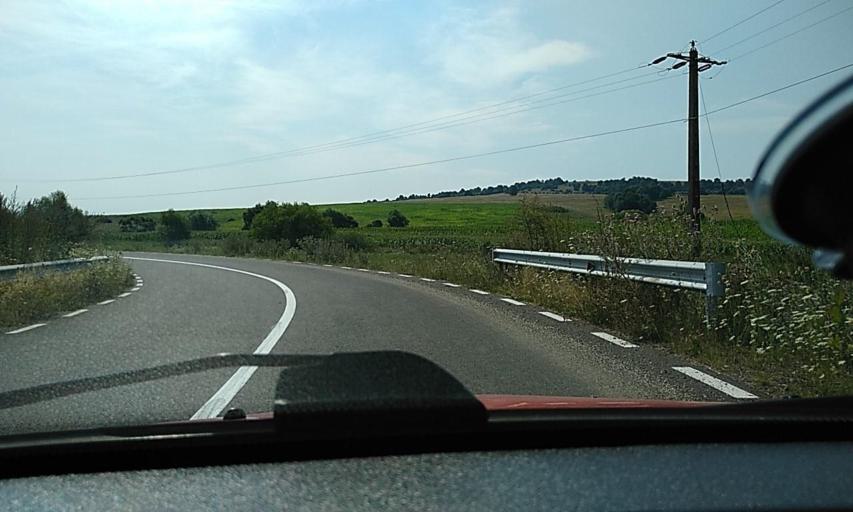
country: RO
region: Brasov
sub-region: Oras Rupea
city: Fiser
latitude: 46.0416
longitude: 25.1213
